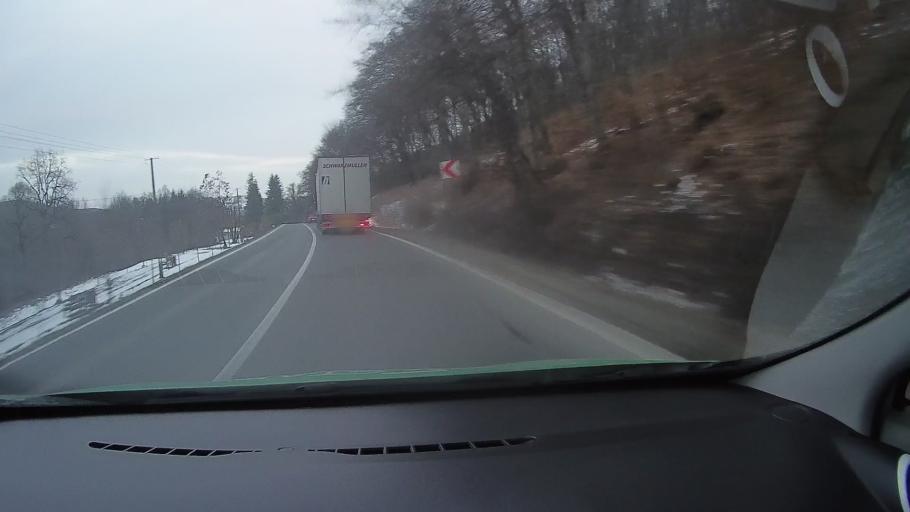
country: RO
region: Harghita
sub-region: Municipiul Odorheiu Secuiesc
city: Odorheiu Secuiesc
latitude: 46.3325
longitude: 25.2723
